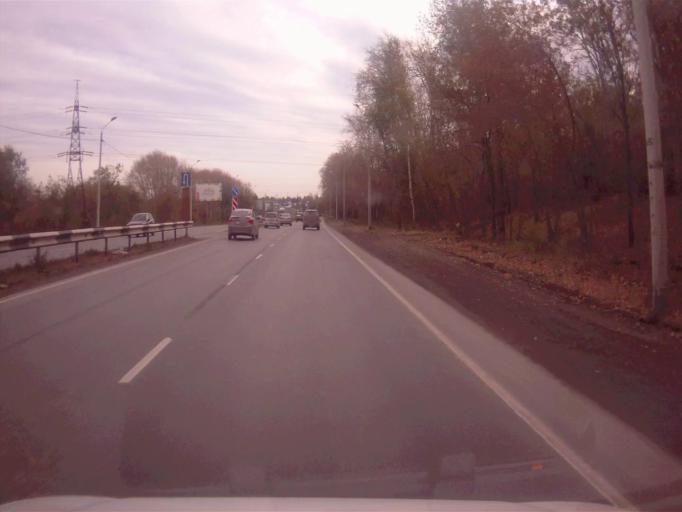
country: RU
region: Chelyabinsk
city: Novosineglazovskiy
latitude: 55.0509
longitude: 61.4125
